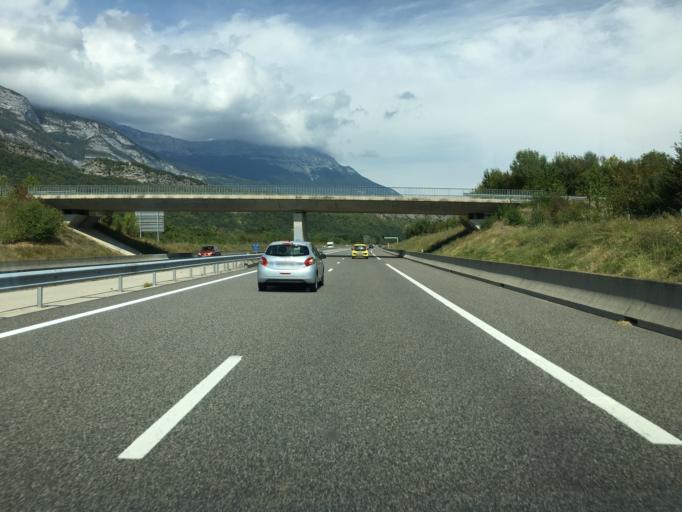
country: FR
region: Rhone-Alpes
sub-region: Departement de l'Isere
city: Vif
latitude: 45.0670
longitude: 5.6814
